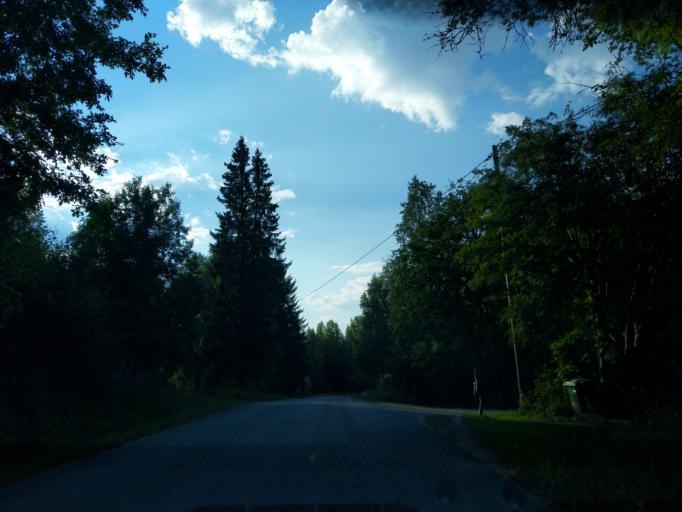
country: FI
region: Satakunta
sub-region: Pori
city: Laengelmaeki
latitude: 61.7849
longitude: 22.2123
